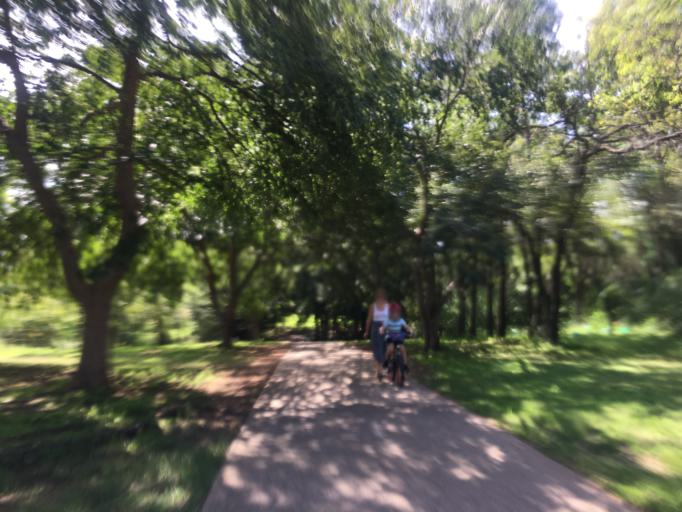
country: AU
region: New South Wales
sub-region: Camden
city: Elderslie
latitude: -34.0636
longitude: 150.6996
